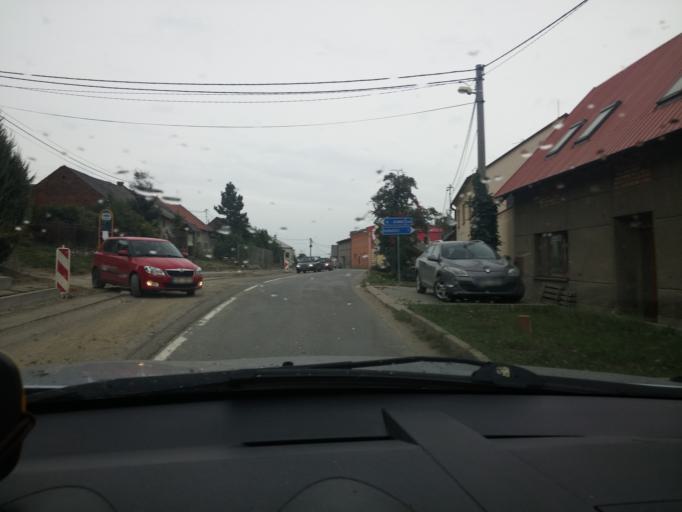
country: CZ
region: Olomoucky
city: Drahanovice
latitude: 49.5789
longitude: 17.0492
